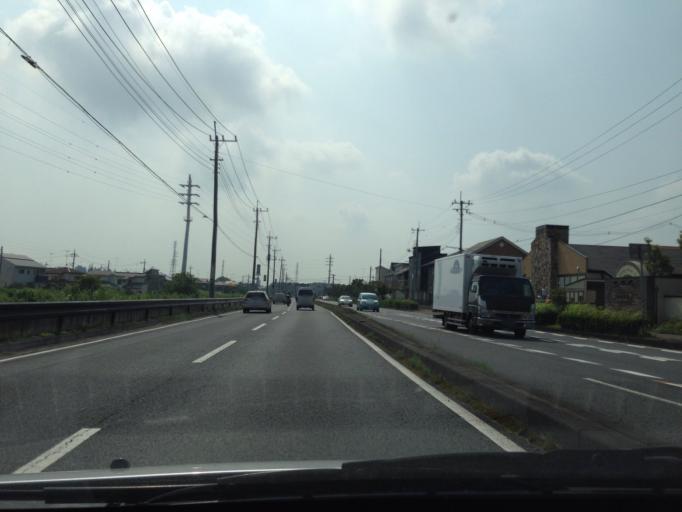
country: JP
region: Ibaraki
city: Ami
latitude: 36.0365
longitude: 140.2191
